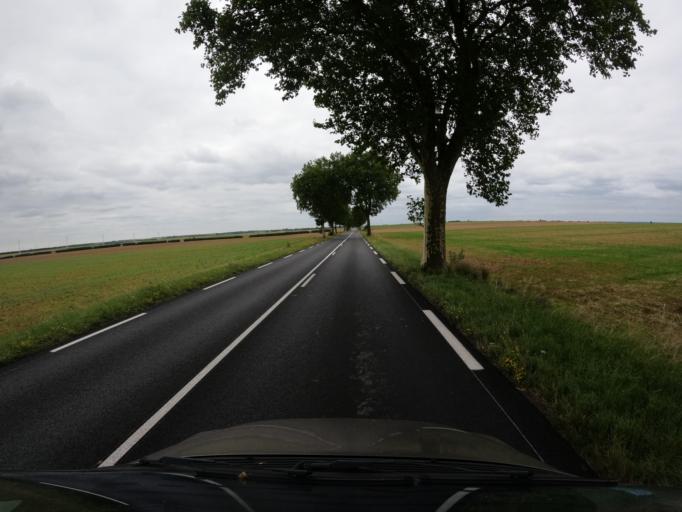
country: FR
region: Pays de la Loire
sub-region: Departement de la Vendee
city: Saint-Martin-sous-Mouzeuil
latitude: 46.5163
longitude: -0.9723
